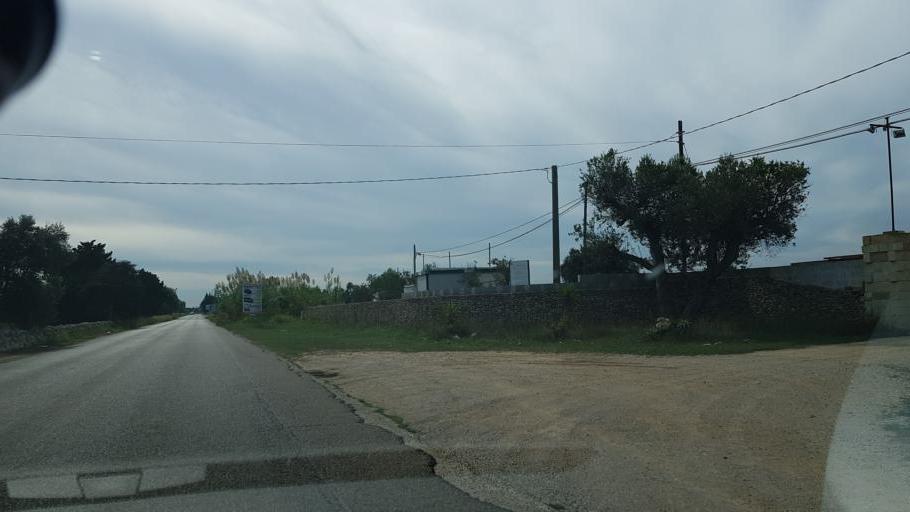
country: IT
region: Apulia
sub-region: Provincia di Lecce
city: Borgagne
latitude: 40.2641
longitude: 18.4327
